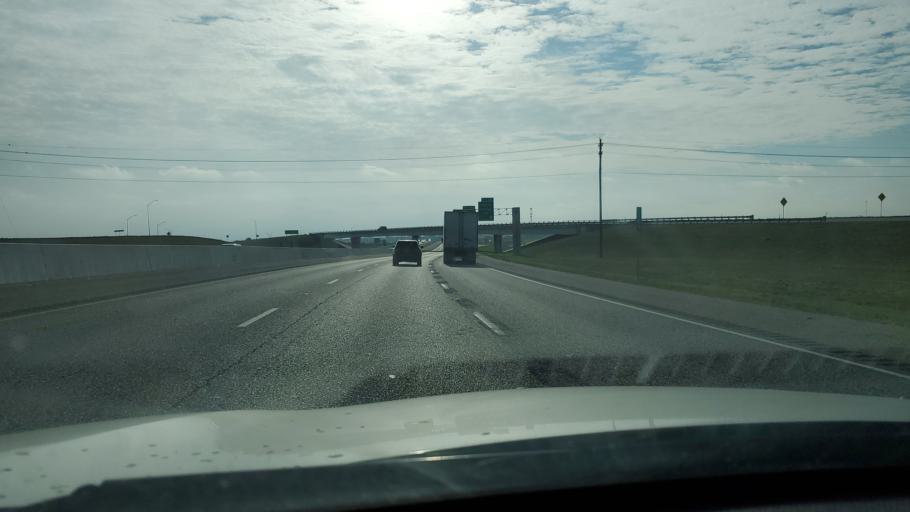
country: US
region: Texas
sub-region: Bell County
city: Fort Hood
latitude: 31.1220
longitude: -97.7754
